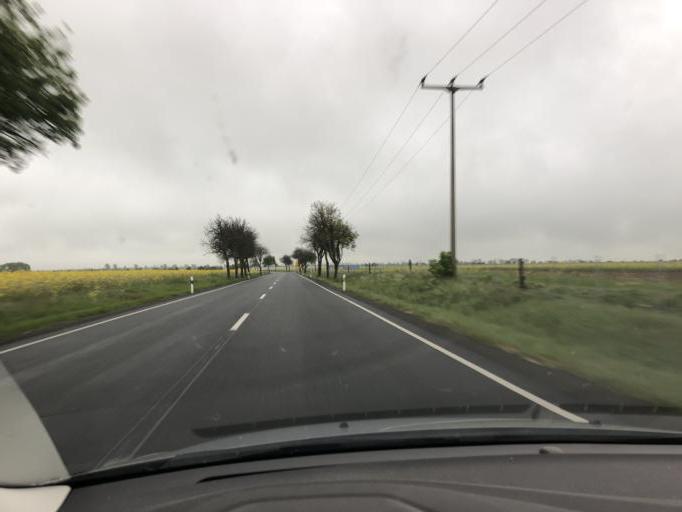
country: DE
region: Saxony
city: Krostitz
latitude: 51.4559
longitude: 12.4917
